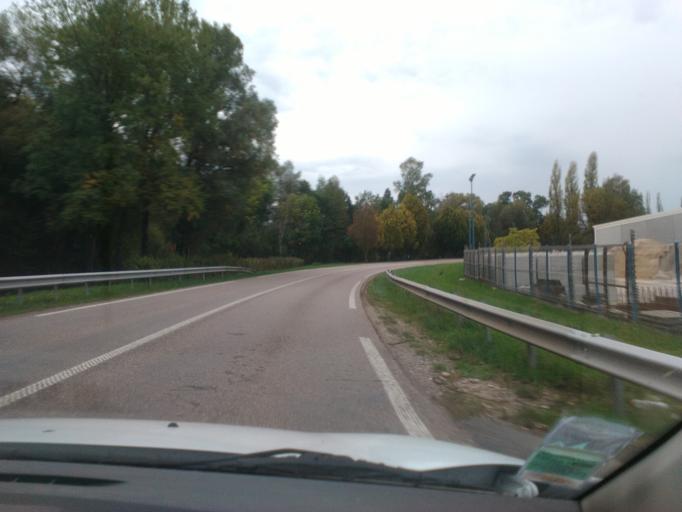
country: FR
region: Lorraine
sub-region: Departement des Vosges
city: Rambervillers
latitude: 48.3347
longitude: 6.6521
